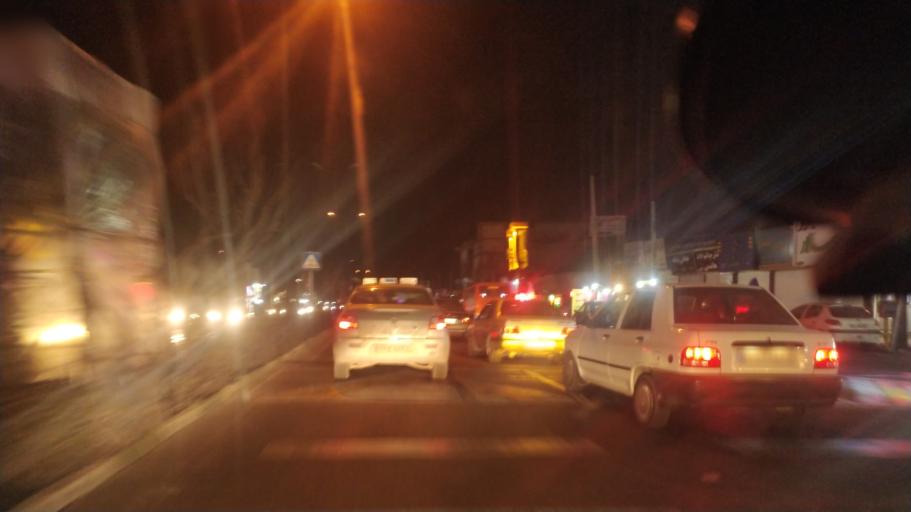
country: IR
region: Alborz
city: Karaj
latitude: 35.7819
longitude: 51.0062
